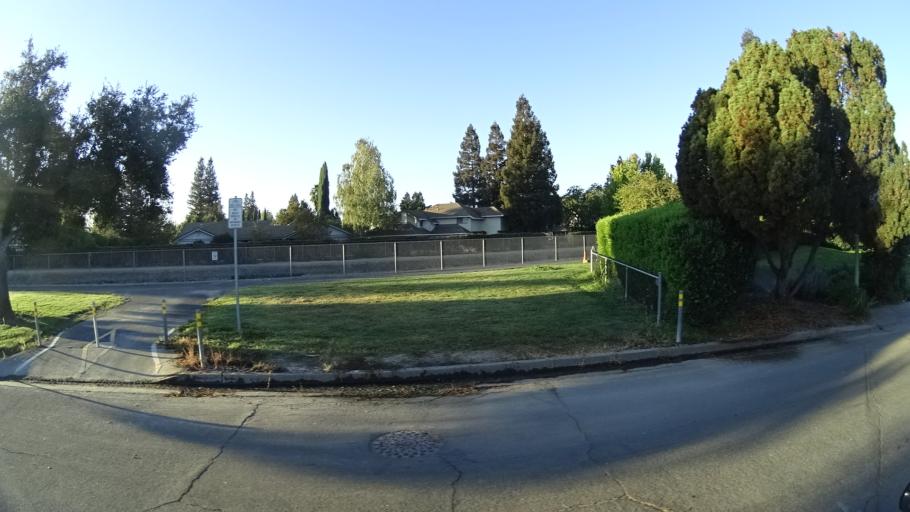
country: US
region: California
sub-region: Sacramento County
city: Parkway
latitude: 38.4983
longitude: -121.5383
